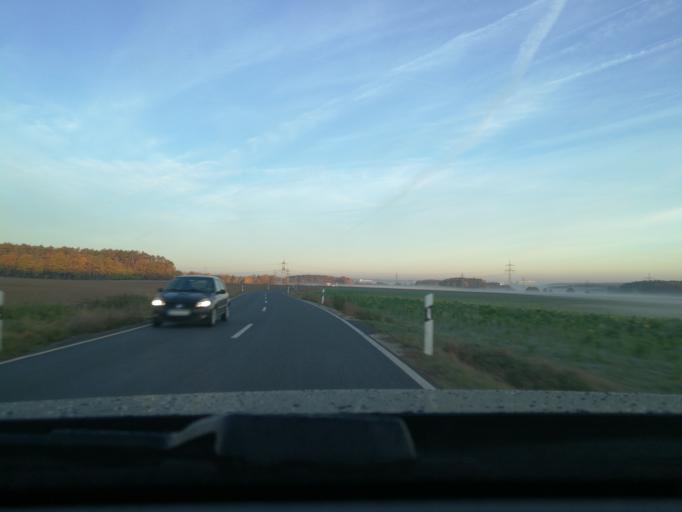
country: DE
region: Bavaria
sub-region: Regierungsbezirk Mittelfranken
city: Obermichelbach
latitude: 49.5447
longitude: 10.9313
